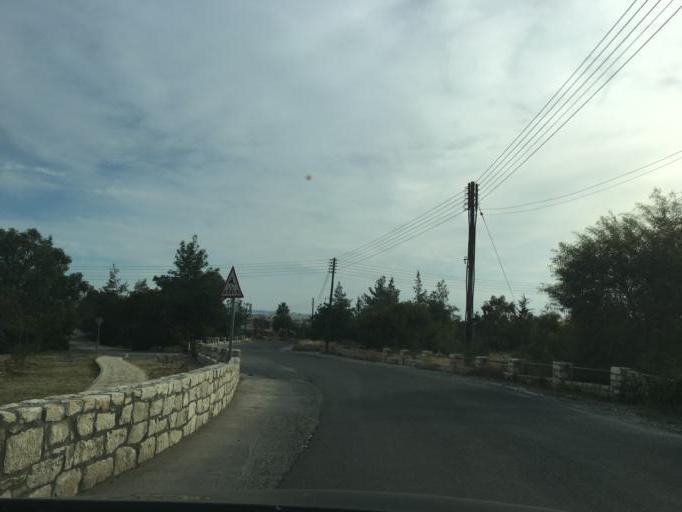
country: CY
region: Limassol
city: Pano Polemidia
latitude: 34.7121
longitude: 33.0053
